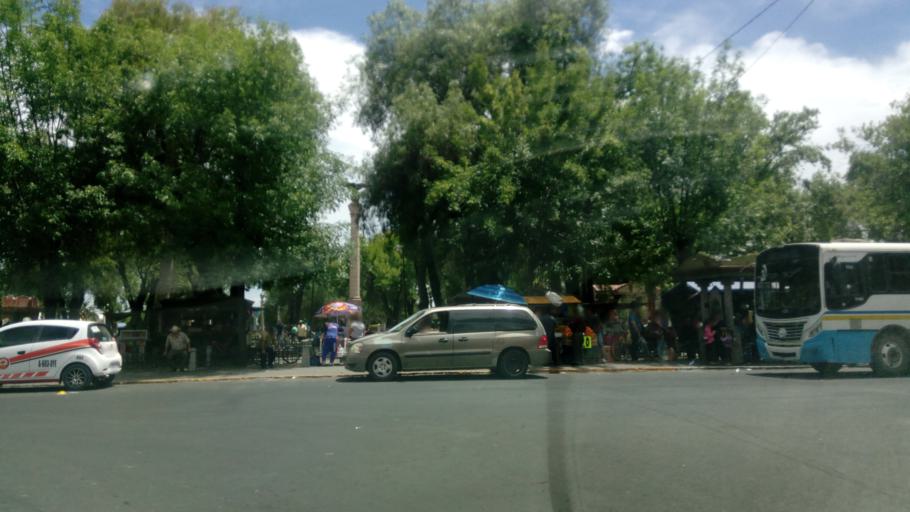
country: MX
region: Durango
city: Victoria de Durango
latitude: 24.0215
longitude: -104.6687
